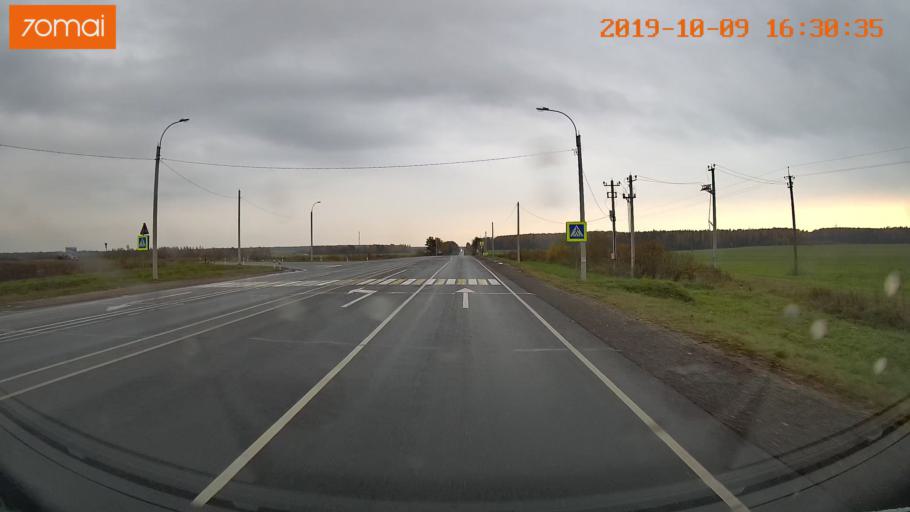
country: RU
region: Kostroma
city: Oktyabr'skiy
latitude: 57.6175
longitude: 40.9417
